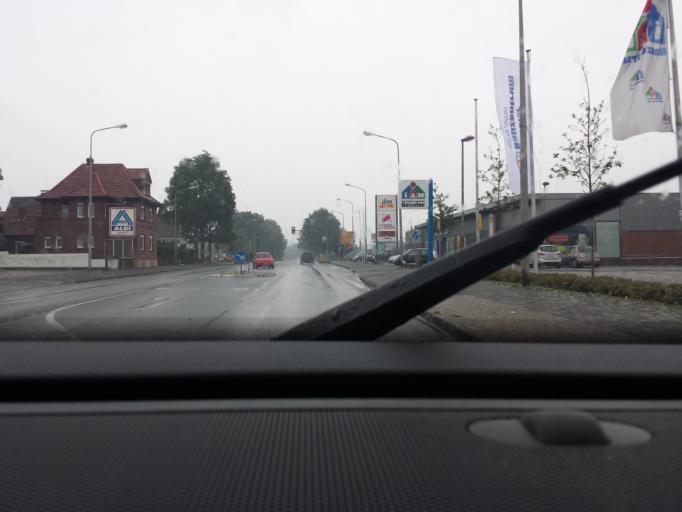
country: DE
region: North Rhine-Westphalia
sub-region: Regierungsbezirk Munster
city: Gronau
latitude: 52.2047
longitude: 7.0521
